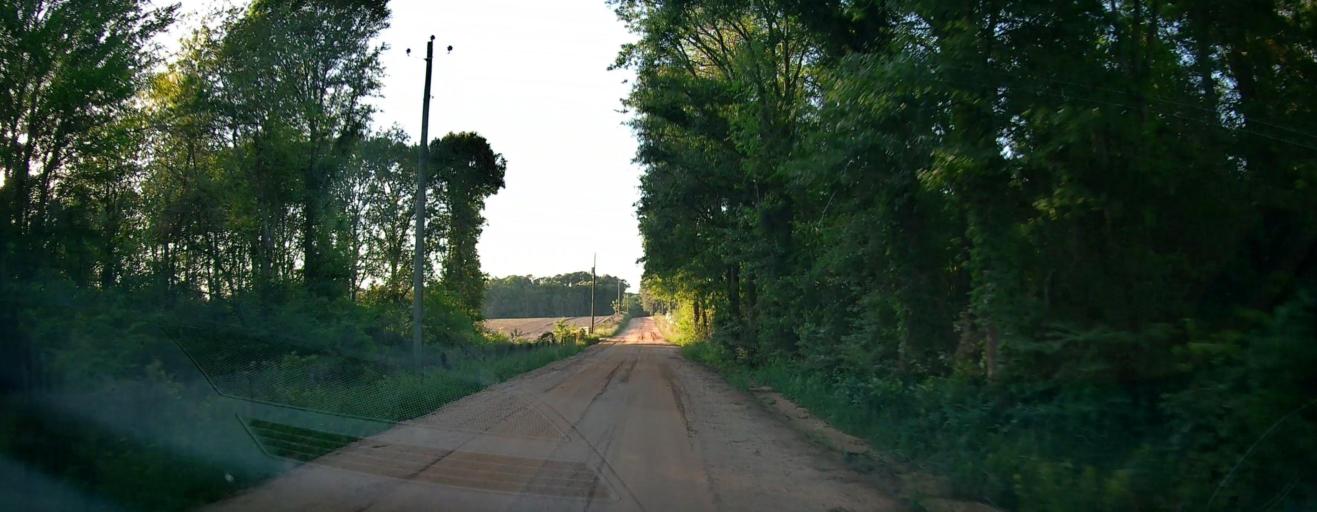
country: US
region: Georgia
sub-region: Irwin County
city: Ocilla
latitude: 31.6448
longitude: -83.2225
